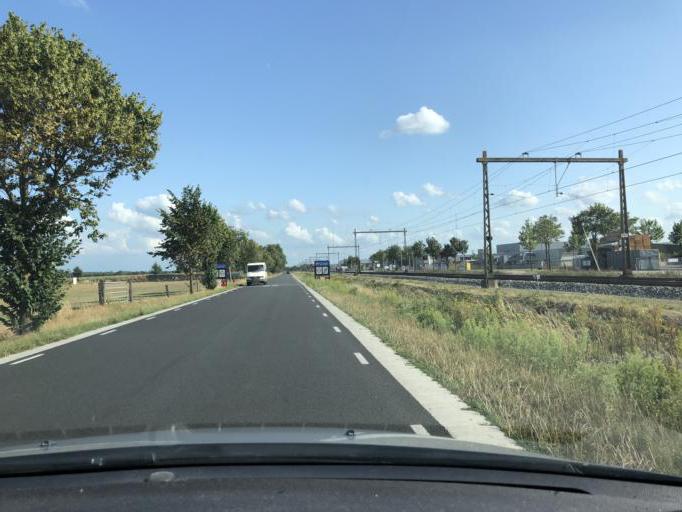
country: NL
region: Overijssel
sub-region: Gemeente Staphorst
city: Staphorst
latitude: 52.6404
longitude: 6.2255
